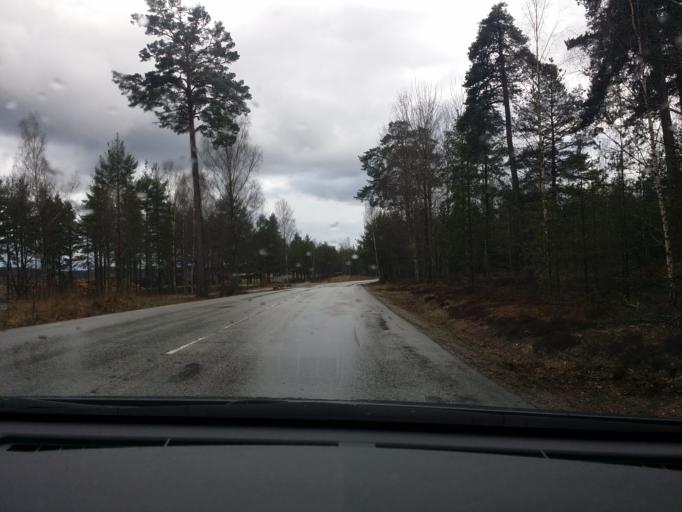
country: SE
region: Soedermanland
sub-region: Eskilstuna Kommun
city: Arla
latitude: 59.3407
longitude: 16.6913
